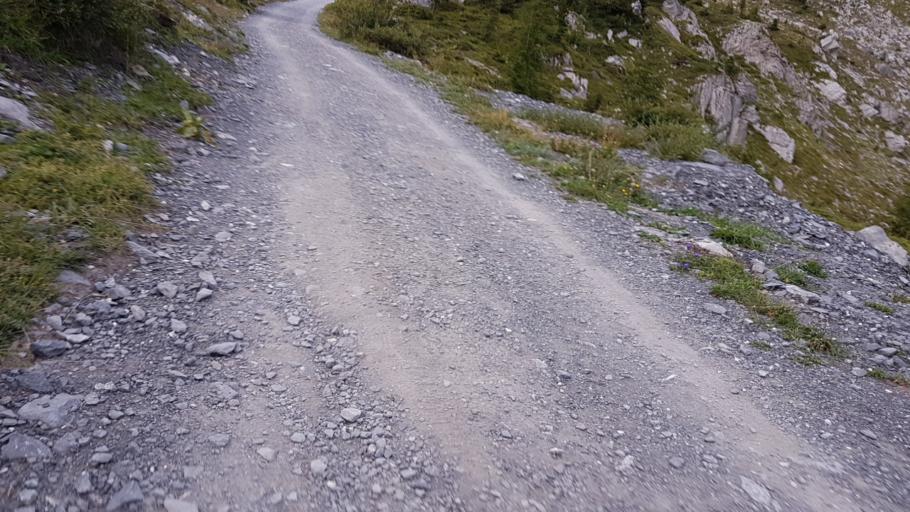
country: CH
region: Valais
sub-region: Leuk District
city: Leukerbad
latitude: 46.4366
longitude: 7.6353
